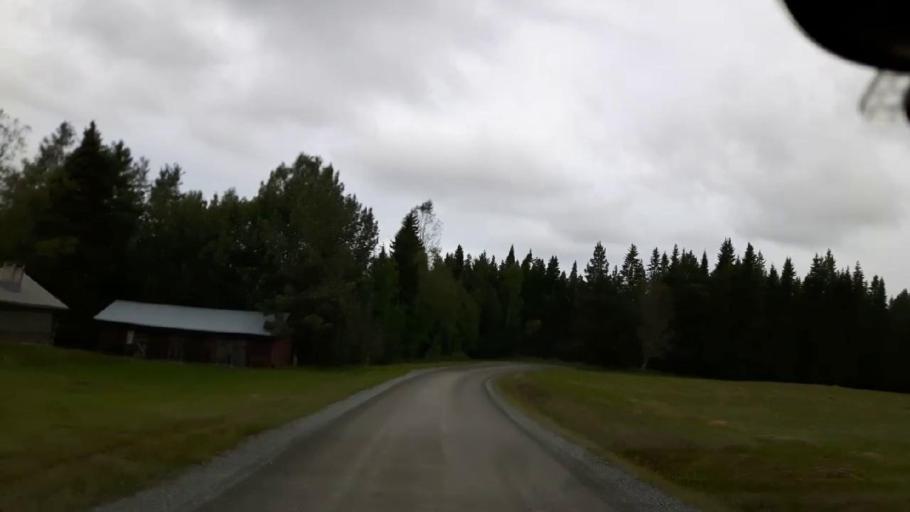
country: SE
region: Jaemtland
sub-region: OEstersunds Kommun
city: Ostersund
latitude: 63.0965
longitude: 14.5467
